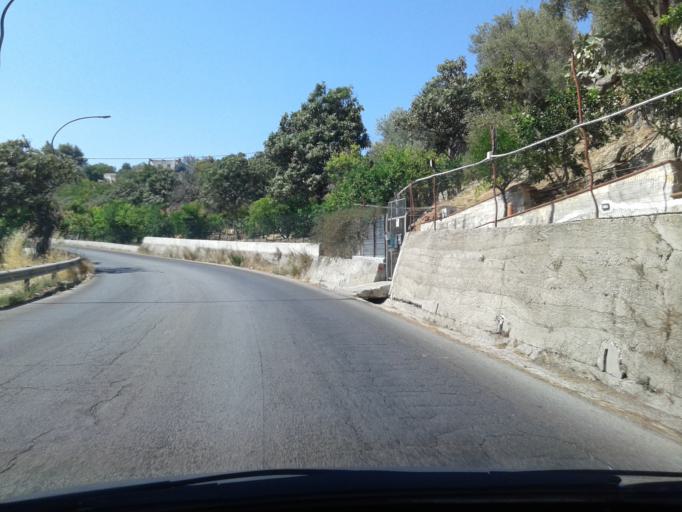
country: IT
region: Sicily
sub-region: Palermo
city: Cannizzaro-Favara
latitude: 38.0745
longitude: 13.2771
